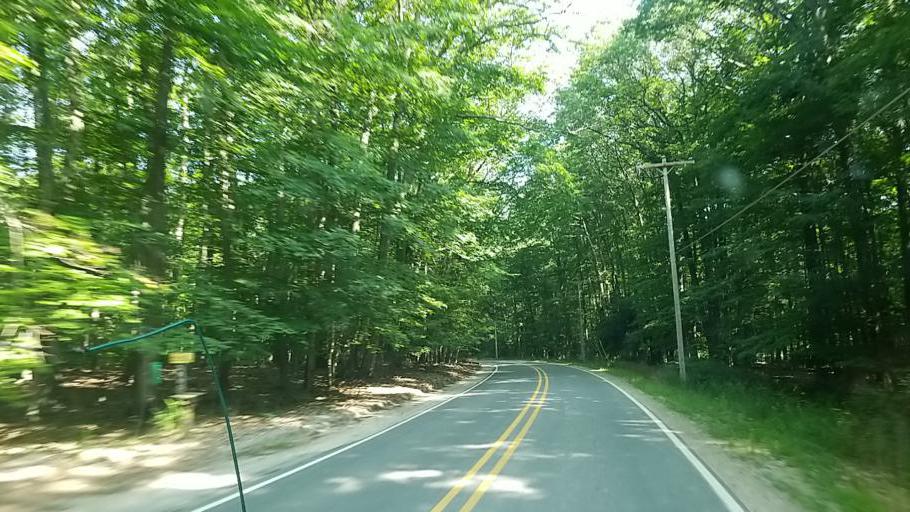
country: US
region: Michigan
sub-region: Muskegon County
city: Whitehall
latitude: 43.3224
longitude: -86.3959
